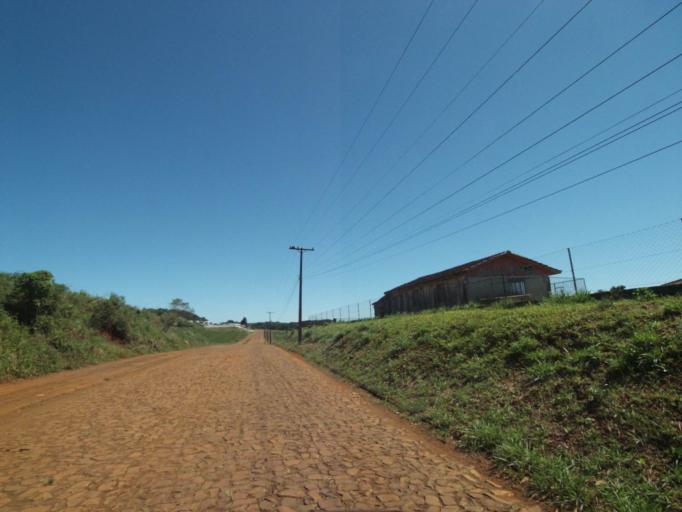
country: BR
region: Parana
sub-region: Pato Branco
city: Pato Branco
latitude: -26.2599
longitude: -52.7820
